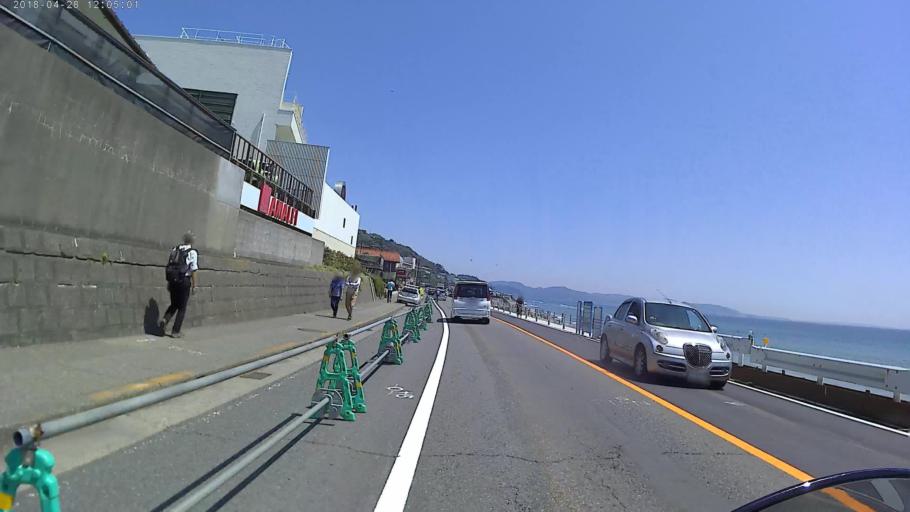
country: JP
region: Kanagawa
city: Kamakura
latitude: 35.3057
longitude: 139.5077
